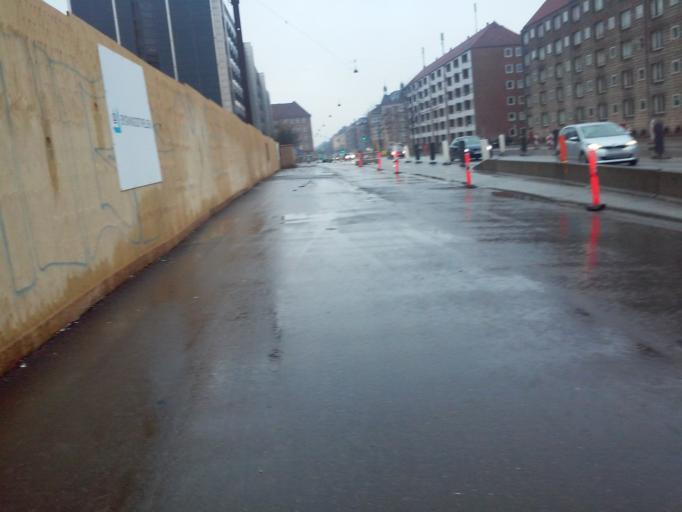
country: DK
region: Capital Region
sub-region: Kobenhavn
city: Copenhagen
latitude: 55.7008
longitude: 12.5564
